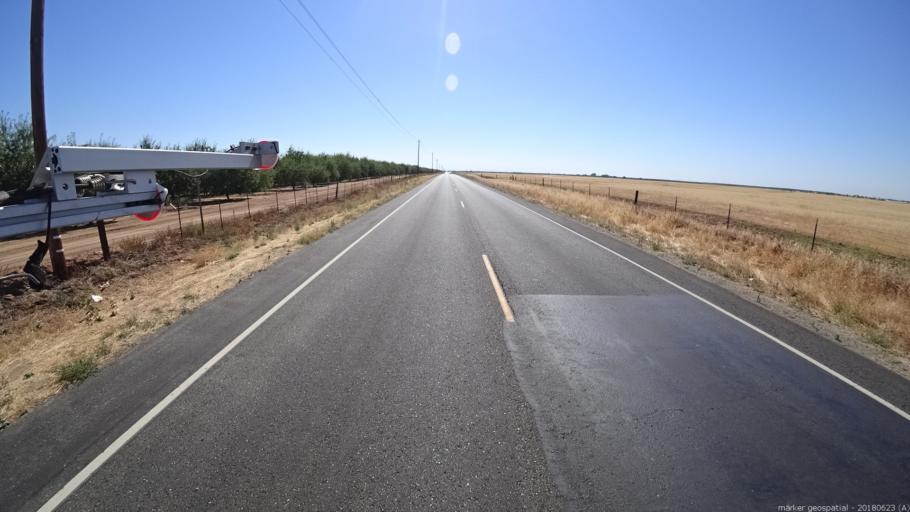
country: US
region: California
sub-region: Madera County
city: Parksdale
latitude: 36.9669
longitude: -119.9930
